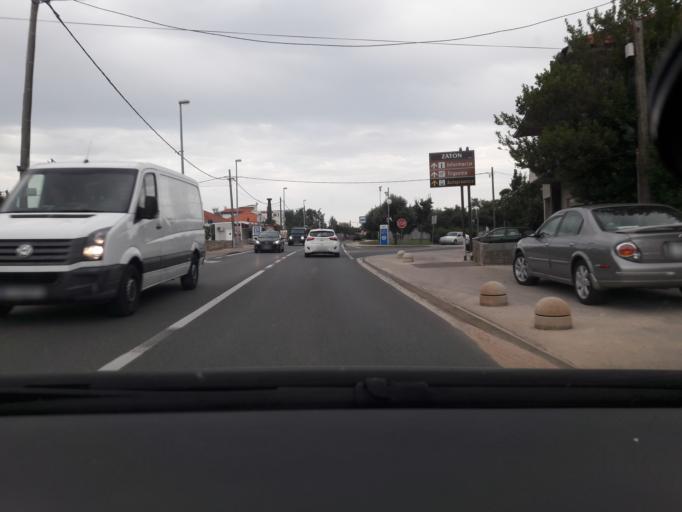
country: HR
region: Zadarska
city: Nin
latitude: 44.2204
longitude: 15.1778
